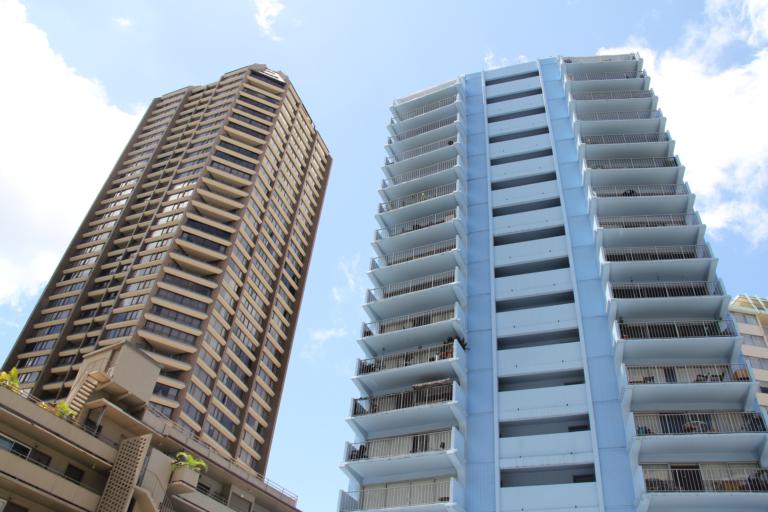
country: US
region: Hawaii
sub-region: Honolulu County
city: Honolulu
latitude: 21.2845
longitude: -157.8373
